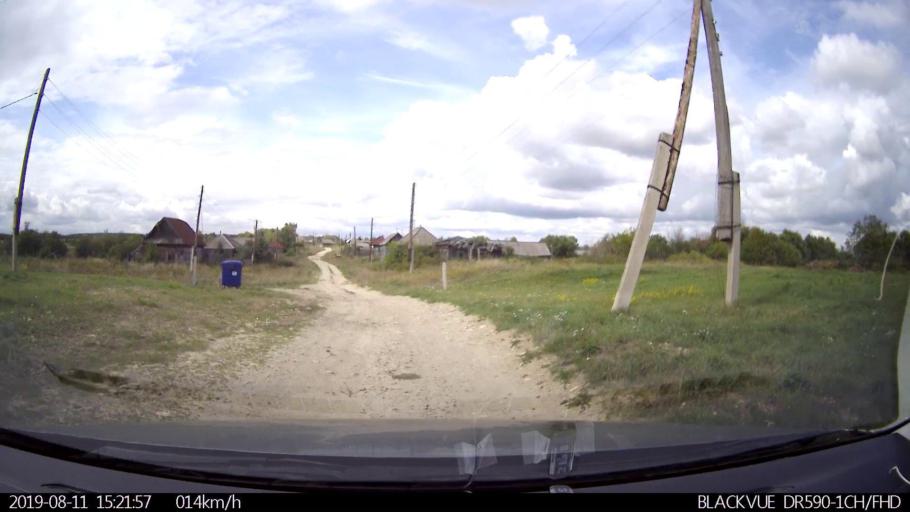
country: RU
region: Ulyanovsk
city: Ignatovka
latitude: 53.8451
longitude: 47.5820
